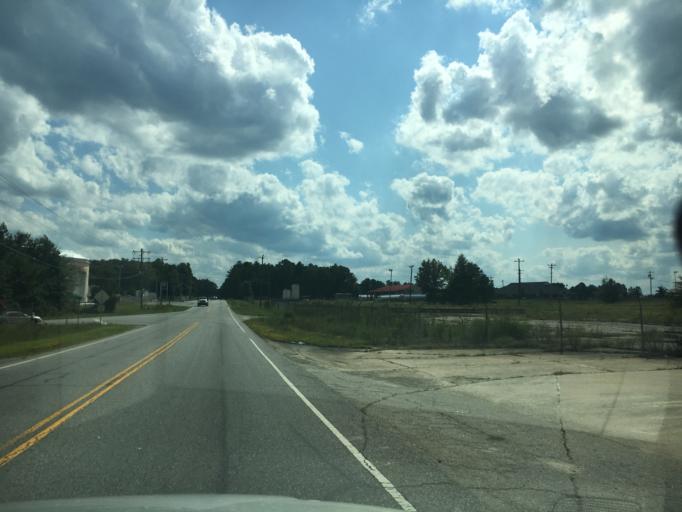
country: US
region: South Carolina
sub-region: Anderson County
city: Belton
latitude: 34.5524
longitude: -82.4920
